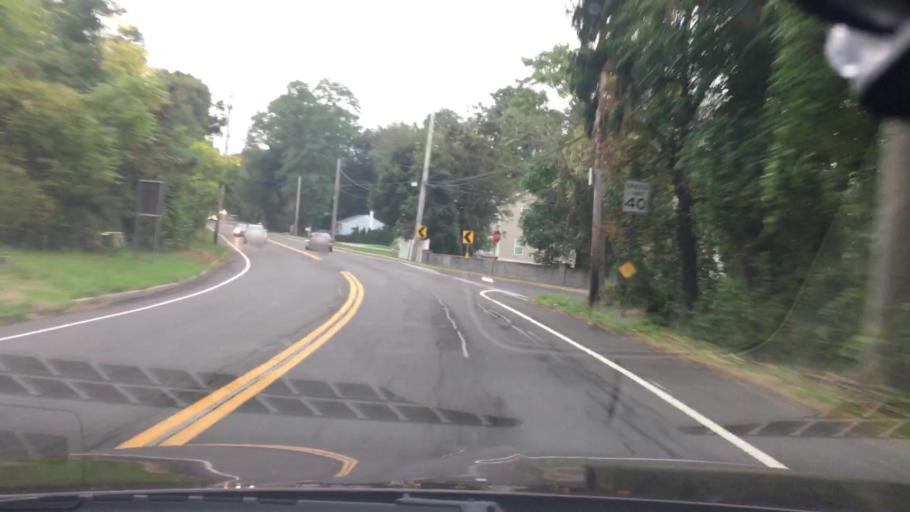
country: US
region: New York
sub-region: Suffolk County
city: Hauppauge
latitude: 40.8206
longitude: -73.2112
